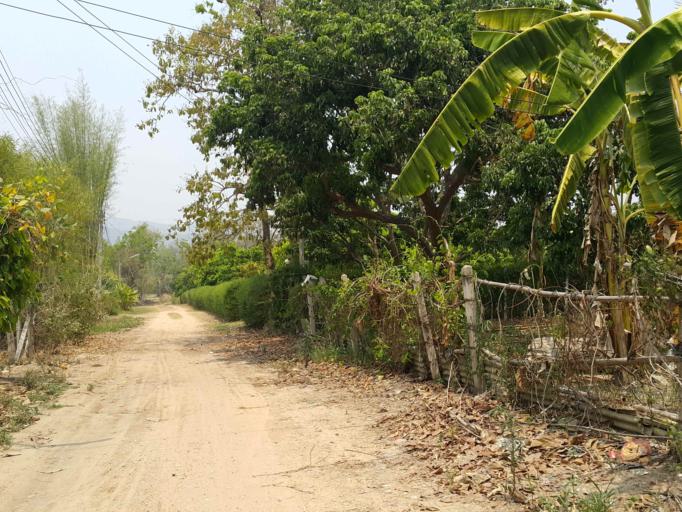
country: TH
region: Chiang Mai
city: San Sai
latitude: 18.9339
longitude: 99.0350
